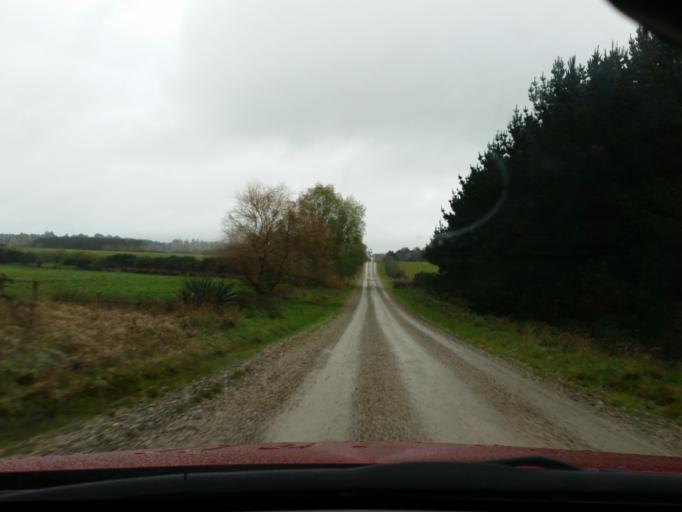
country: NZ
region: Southland
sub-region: Invercargill City
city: Invercargill
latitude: -46.2850
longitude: 168.5197
